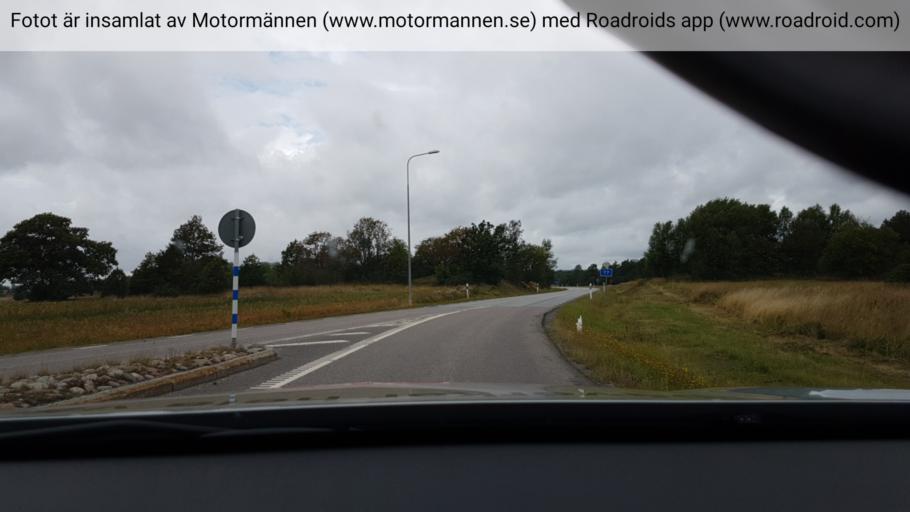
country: SE
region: Stockholm
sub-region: Vallentuna Kommun
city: Vallentuna
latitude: 59.7519
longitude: 18.0432
